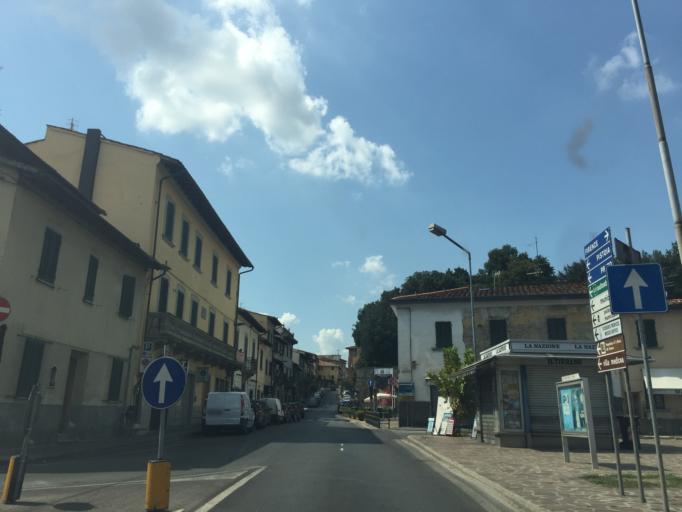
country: IT
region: Tuscany
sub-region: Provincia di Prato
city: Poggio A Caiano
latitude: 43.8155
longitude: 11.0585
